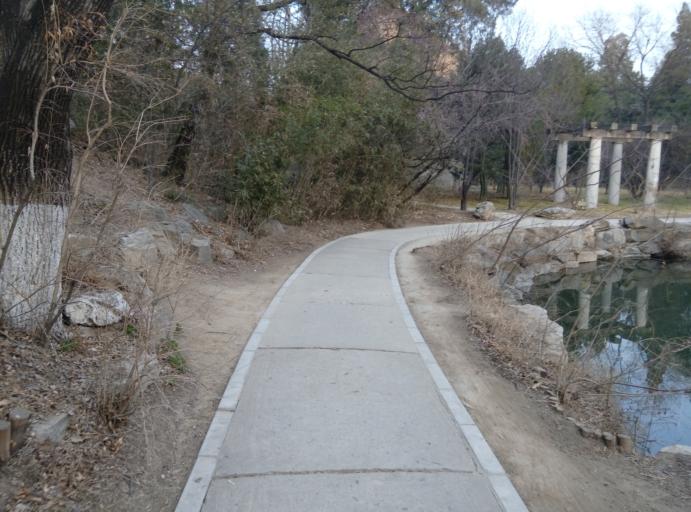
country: CN
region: Beijing
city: Haidian
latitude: 39.9923
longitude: 116.3036
